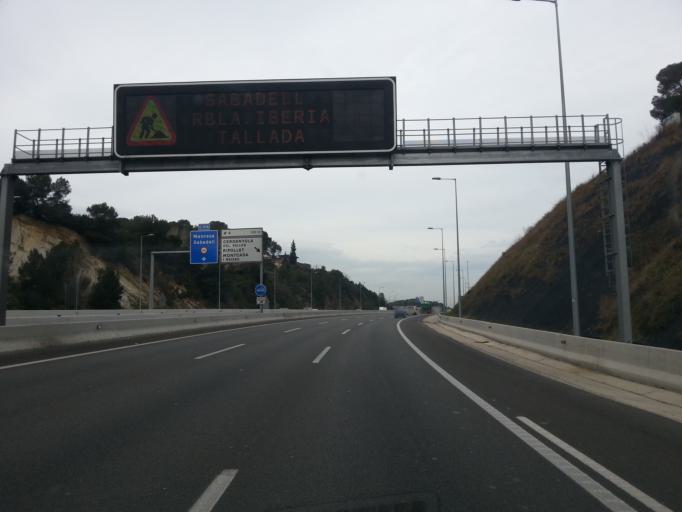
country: ES
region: Catalonia
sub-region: Provincia de Barcelona
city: Montcada i Reixac
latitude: 41.4731
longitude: 2.1634
